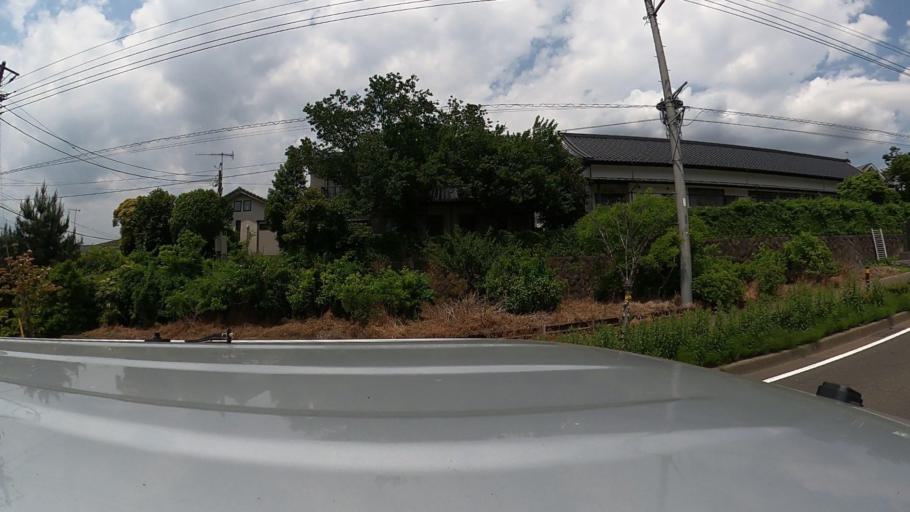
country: JP
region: Kanagawa
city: Chigasaki
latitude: 35.3934
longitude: 139.4186
